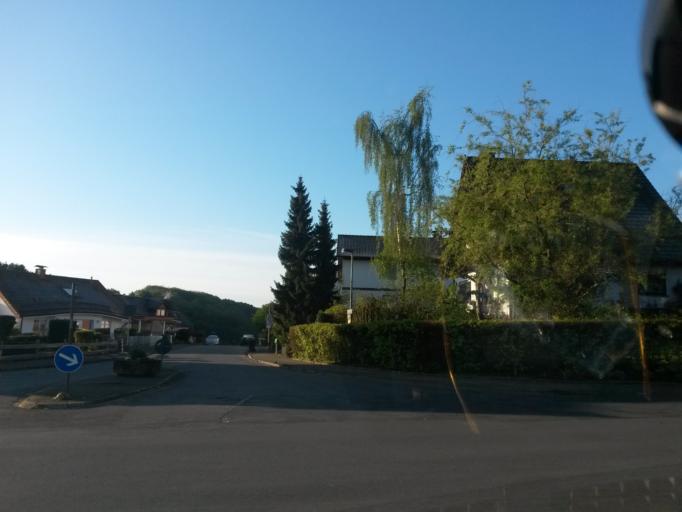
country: DE
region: North Rhine-Westphalia
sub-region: Regierungsbezirk Arnsberg
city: Herscheid
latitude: 51.1229
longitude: 7.7608
